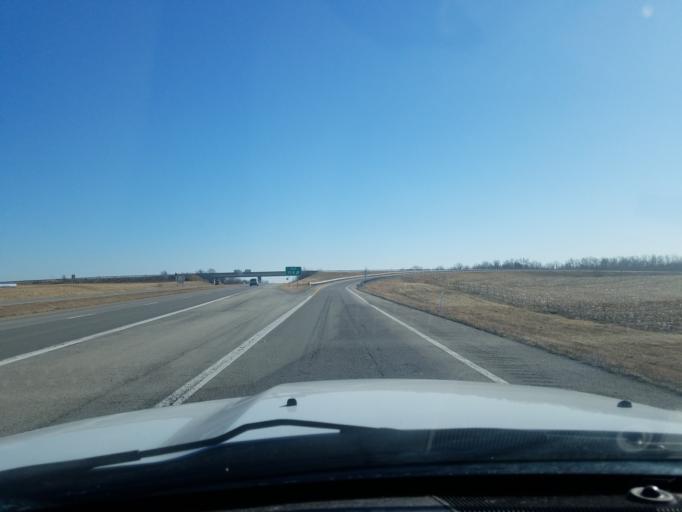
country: US
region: Kentucky
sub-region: Henderson County
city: Henderson
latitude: 37.7997
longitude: -87.5603
